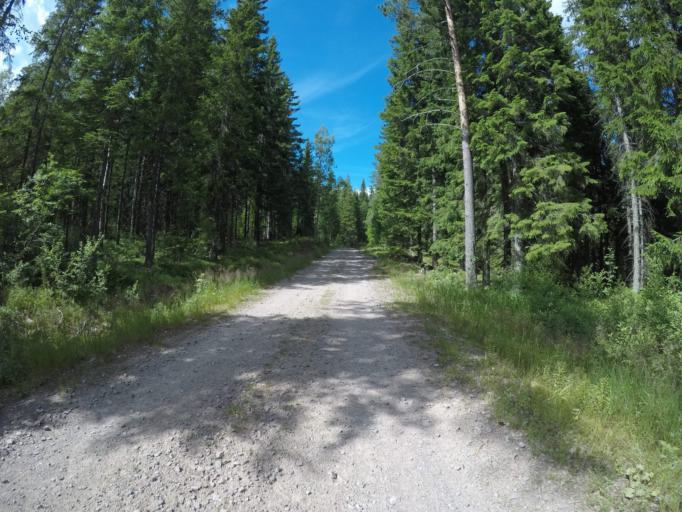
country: SE
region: OErebro
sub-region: Hallefors Kommun
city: Haellefors
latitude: 60.0726
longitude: 14.4649
